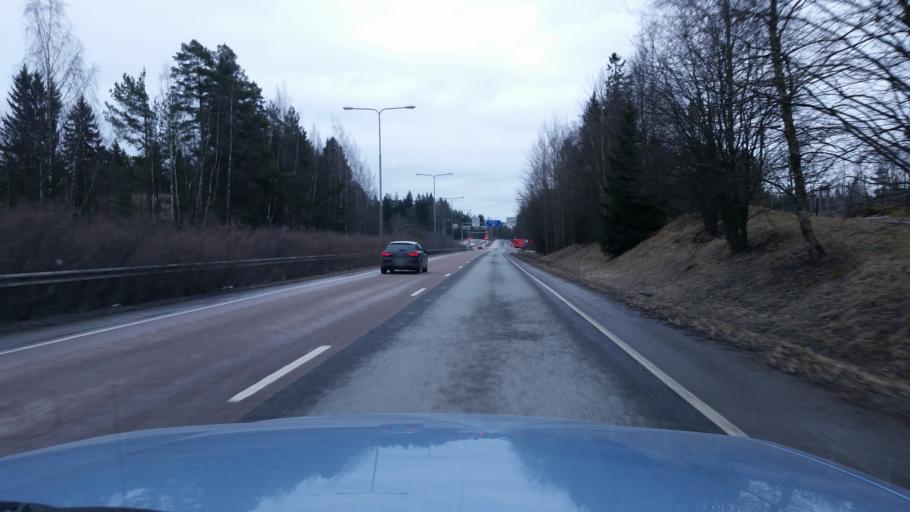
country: FI
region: Uusimaa
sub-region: Helsinki
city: Kilo
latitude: 60.2559
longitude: 24.8194
